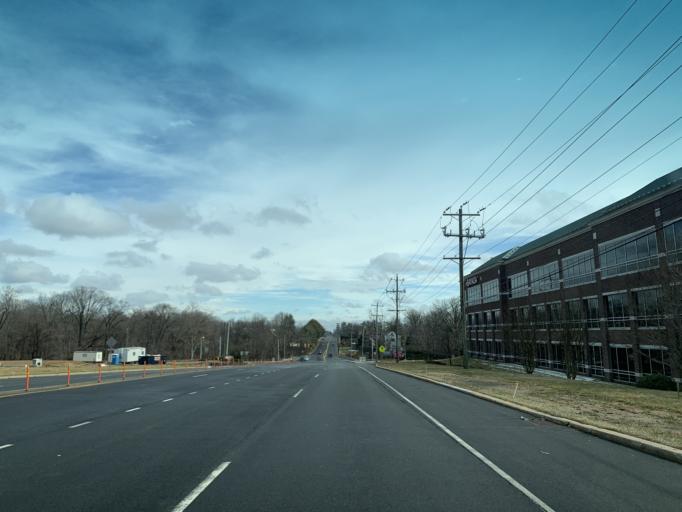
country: US
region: Delaware
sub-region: New Castle County
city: Elsmere
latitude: 39.7579
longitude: -75.6022
